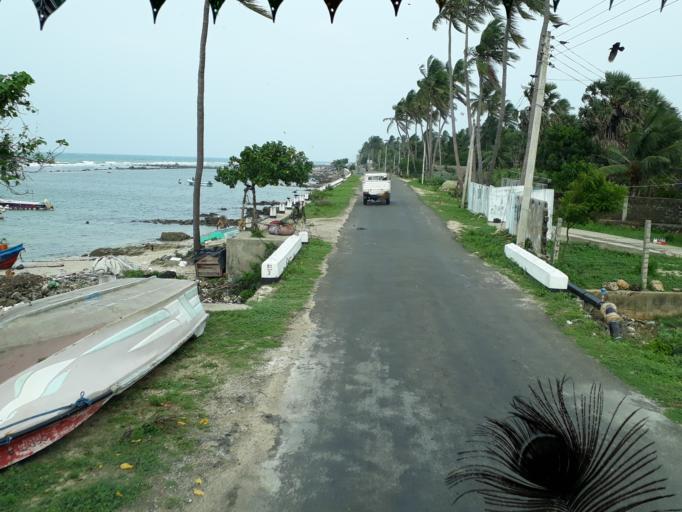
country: LK
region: Northern Province
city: Point Pedro
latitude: 9.8325
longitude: 80.2027
